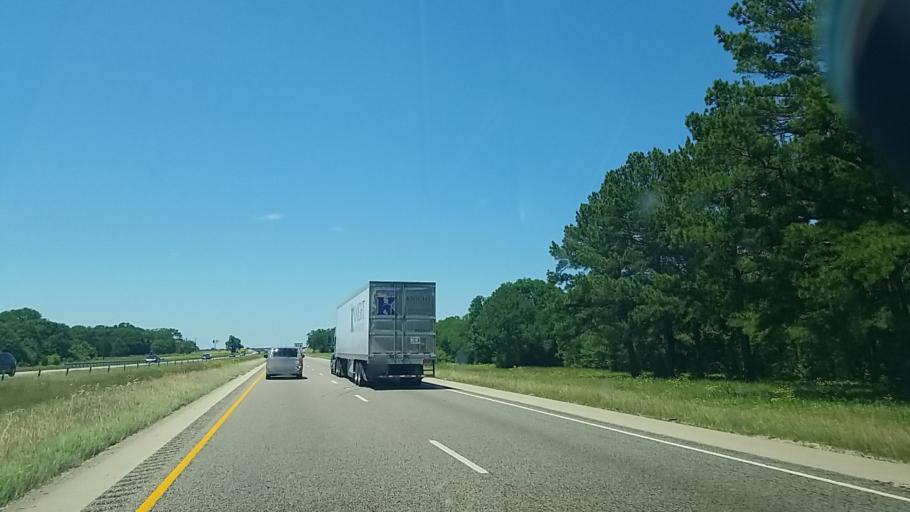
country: US
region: Texas
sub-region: Madison County
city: Madisonville
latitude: 31.0839
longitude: -95.9580
